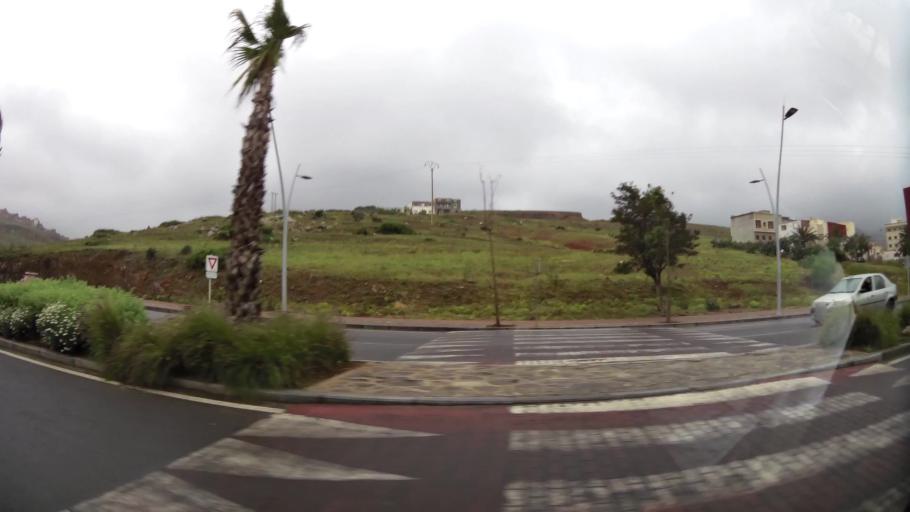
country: MA
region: Oriental
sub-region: Nador
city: Nador
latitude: 35.1916
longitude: -2.9311
